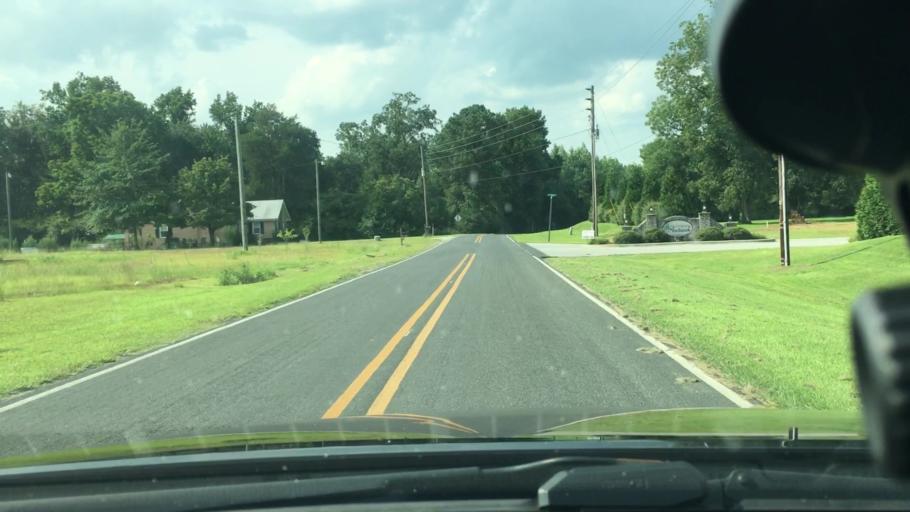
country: US
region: North Carolina
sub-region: Craven County
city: New Bern
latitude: 35.1835
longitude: -77.0579
